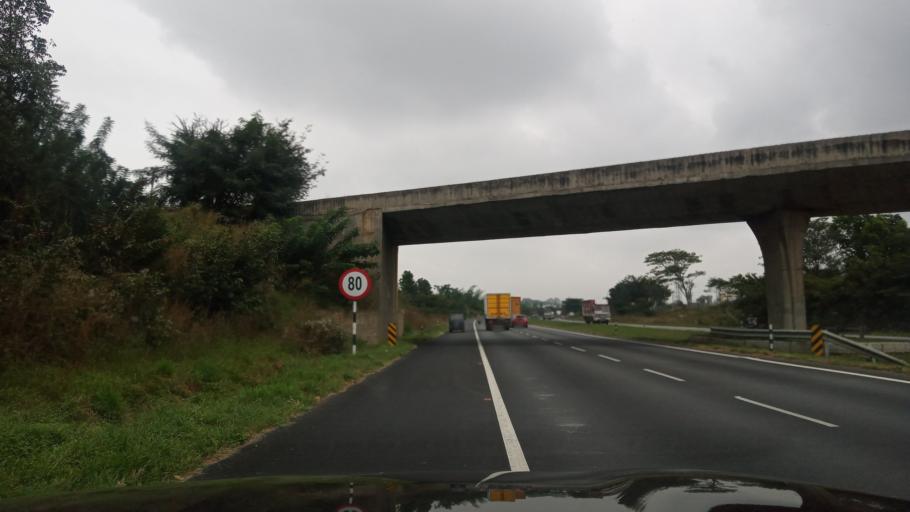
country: IN
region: Karnataka
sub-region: Bangalore Urban
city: Bangalore
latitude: 12.8640
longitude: 77.6251
